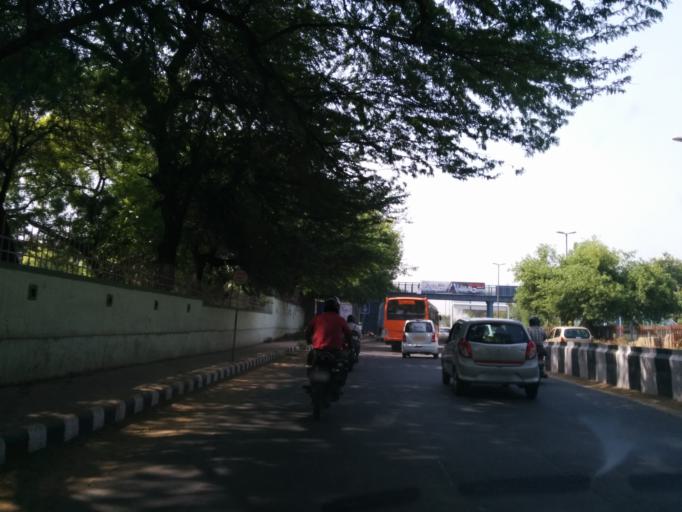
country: IN
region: NCT
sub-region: New Delhi
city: New Delhi
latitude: 28.5647
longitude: 77.2078
